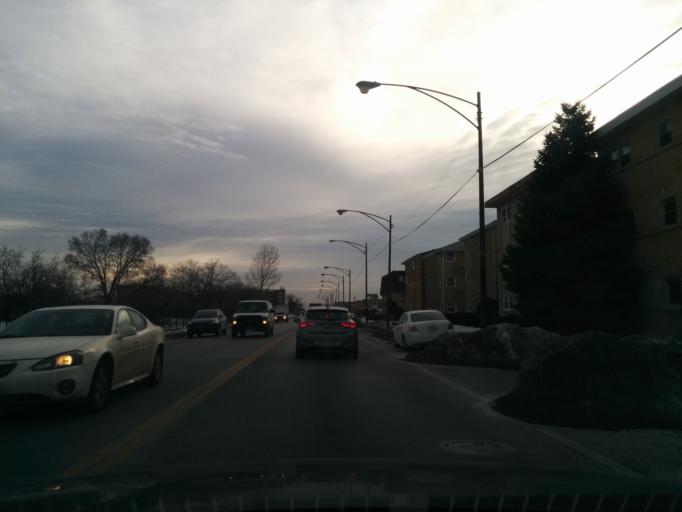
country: US
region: Illinois
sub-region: Cook County
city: Harwood Heights
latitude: 41.9528
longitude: -87.7954
